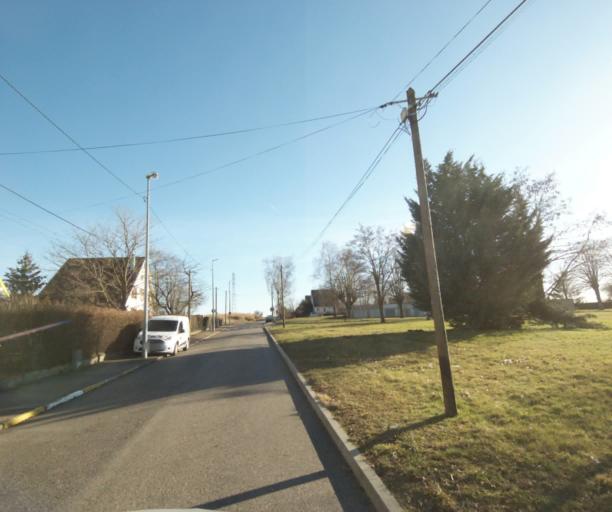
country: FR
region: Lorraine
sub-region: Departement de Meurthe-et-Moselle
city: Art-sur-Meurthe
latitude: 48.6370
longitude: 6.2703
